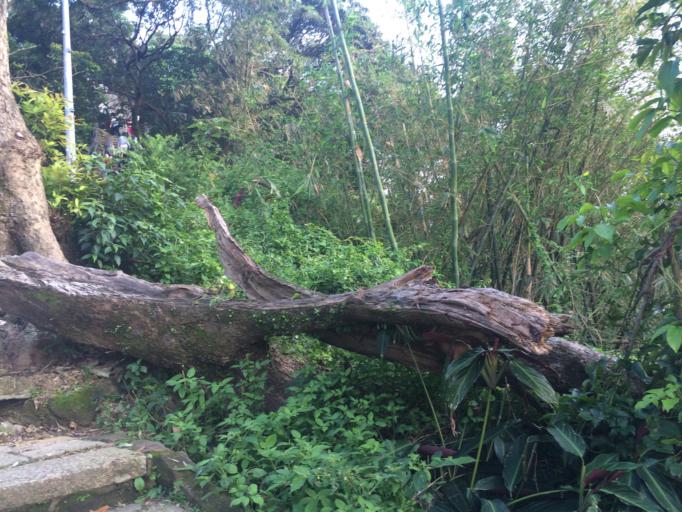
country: TW
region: Taipei
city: Taipei
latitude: 25.0271
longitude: 121.5738
